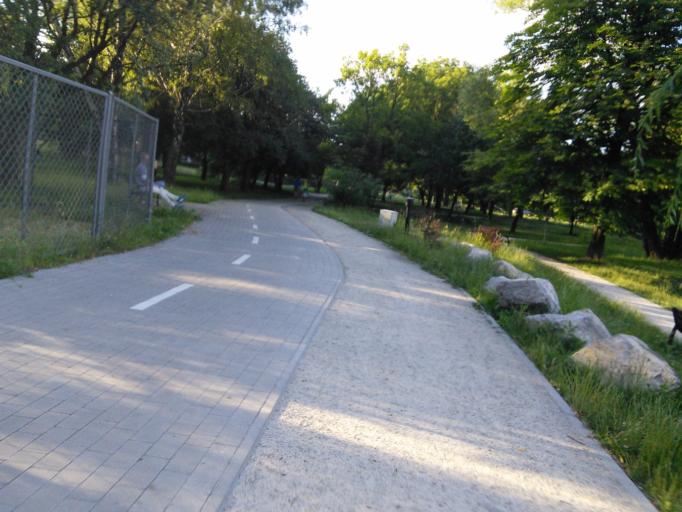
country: PL
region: Silesian Voivodeship
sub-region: Bytom
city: Bytom
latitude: 50.3544
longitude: 18.9019
